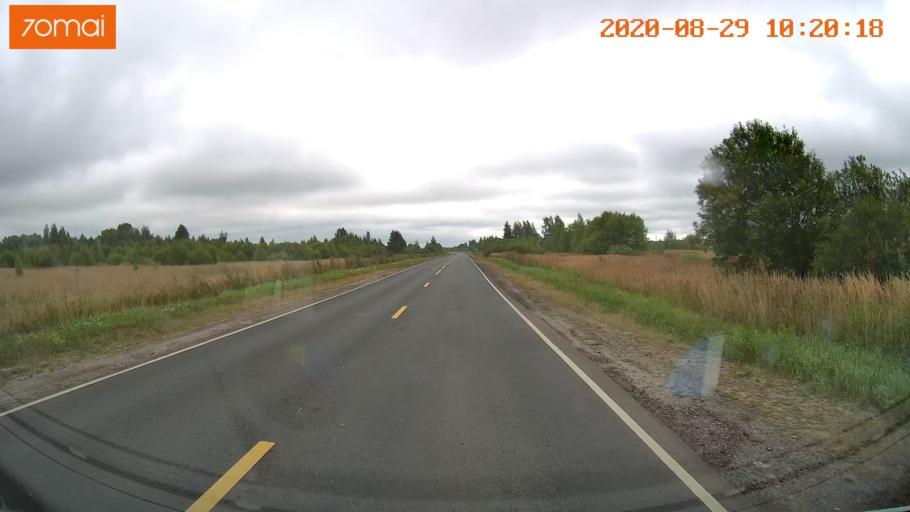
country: RU
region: Ivanovo
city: Yur'yevets
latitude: 57.3242
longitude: 42.8818
